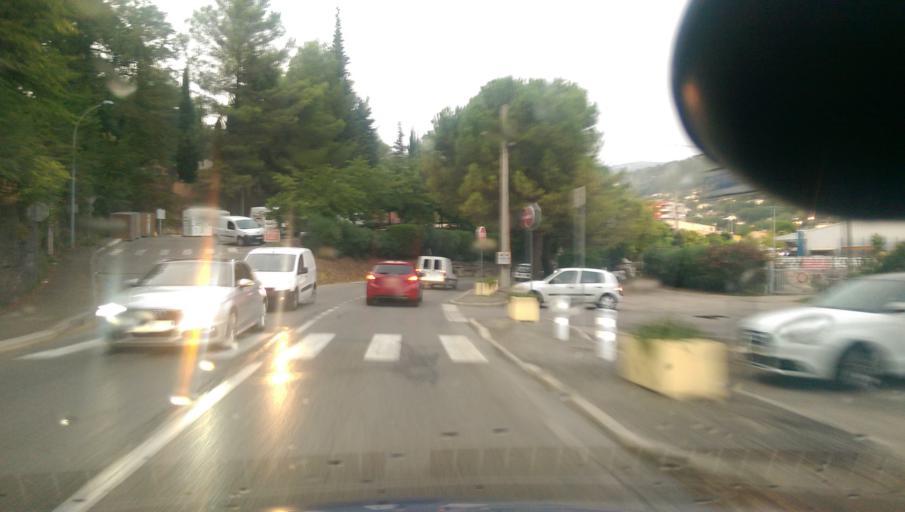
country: FR
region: Provence-Alpes-Cote d'Azur
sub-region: Departement des Alpes-Maritimes
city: Opio
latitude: 43.6762
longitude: 6.9756
